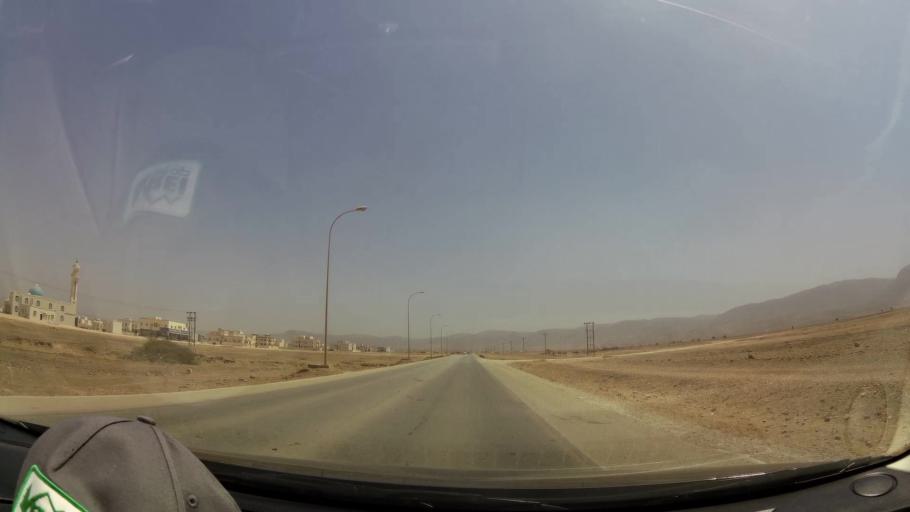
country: OM
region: Zufar
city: Salalah
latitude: 17.0809
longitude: 54.2170
